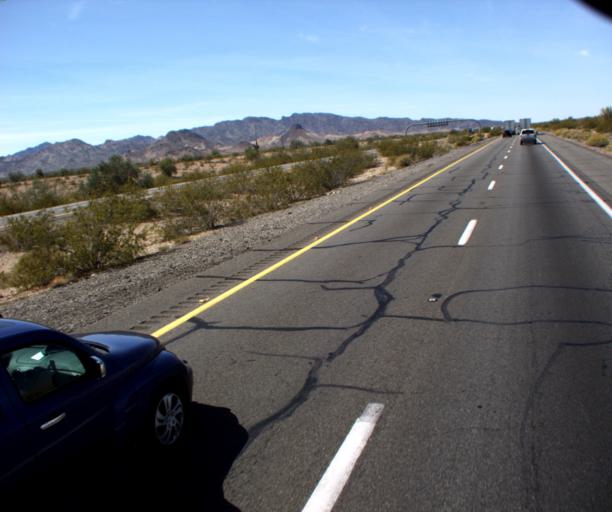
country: US
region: Arizona
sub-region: La Paz County
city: Quartzsite
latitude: 33.6556
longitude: -114.2709
